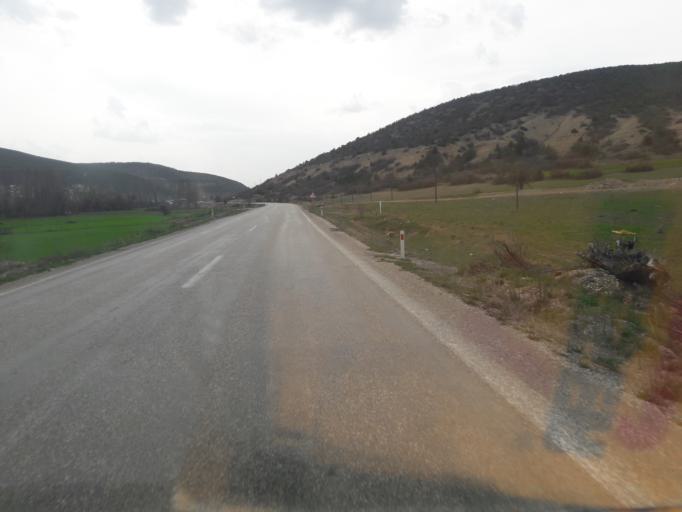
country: TR
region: Gumushane
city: Siran
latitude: 40.1771
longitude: 39.1437
